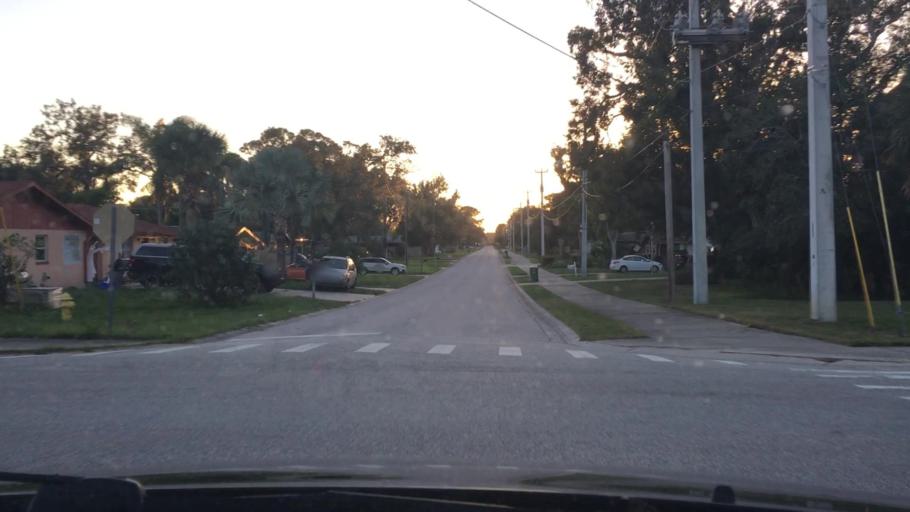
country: US
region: Florida
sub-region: Volusia County
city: Ormond Beach
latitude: 29.3005
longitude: -81.0666
